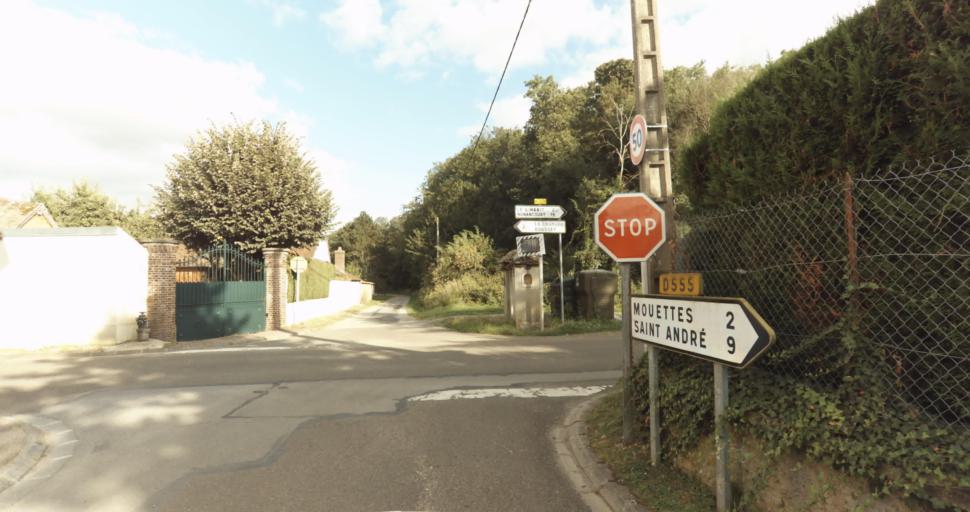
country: FR
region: Haute-Normandie
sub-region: Departement de l'Eure
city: La Couture-Boussey
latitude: 48.8878
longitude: 1.3817
